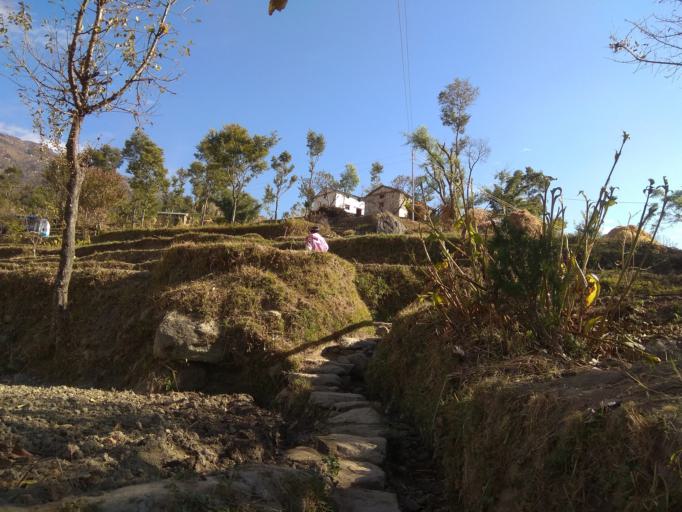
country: NP
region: Far Western
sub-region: Seti Zone
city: Achham
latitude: 29.2452
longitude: 81.6247
